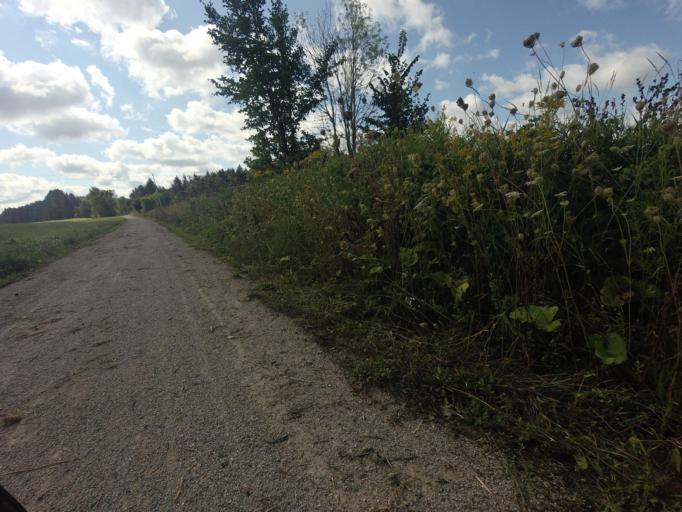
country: CA
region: Ontario
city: Huron East
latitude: 43.7267
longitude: -81.4106
